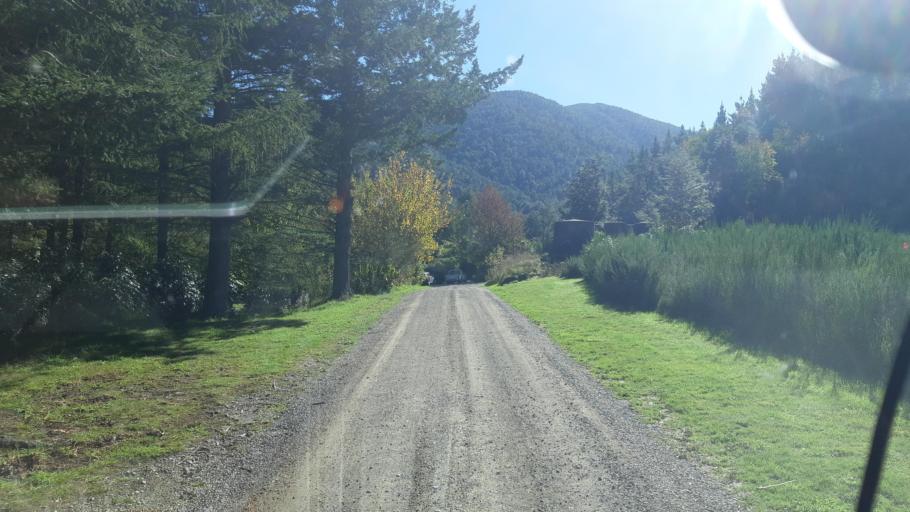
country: NZ
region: Canterbury
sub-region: Waimakariri District
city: Oxford
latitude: -43.1932
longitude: 172.3368
